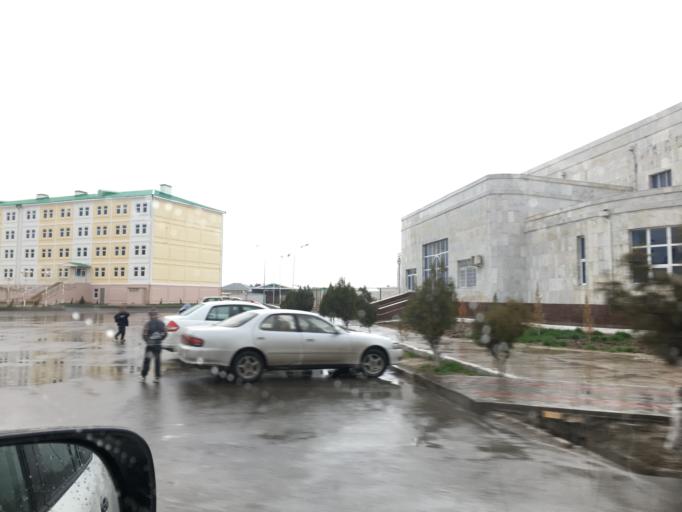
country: TM
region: Mary
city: Mary
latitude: 37.5799
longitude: 61.8344
